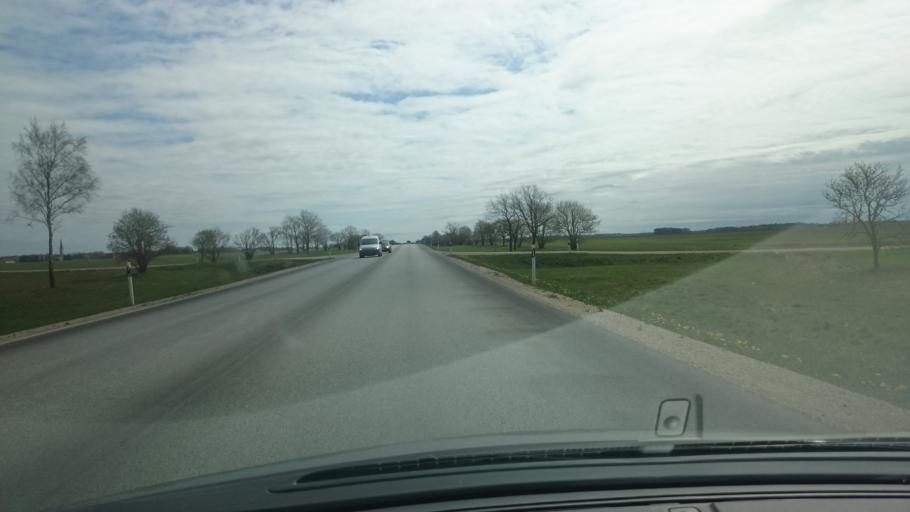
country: EE
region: Laeaene-Virumaa
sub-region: Haljala vald
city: Haljala
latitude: 59.4279
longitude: 26.2347
